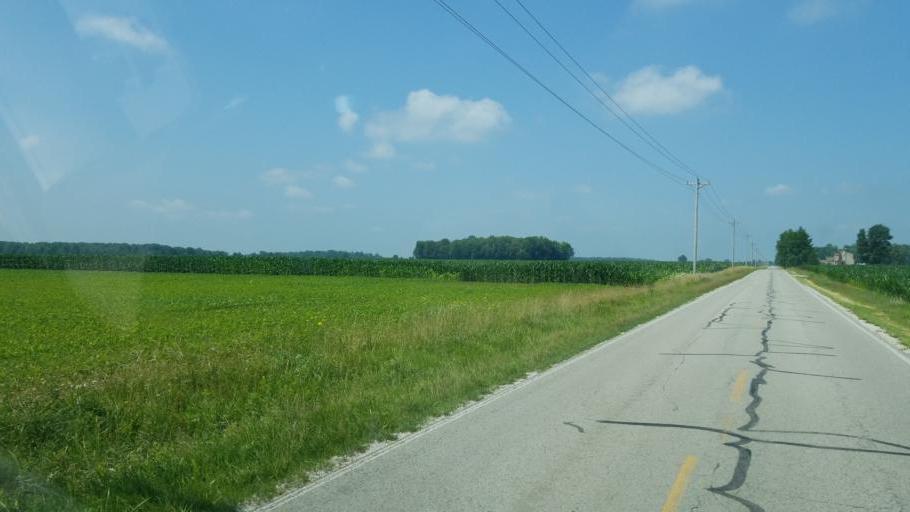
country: US
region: Ohio
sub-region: Huron County
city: Willard
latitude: 40.9937
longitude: -82.8830
